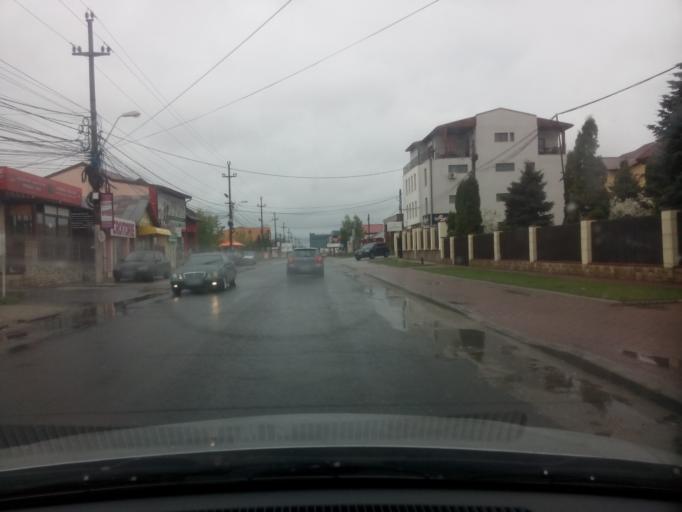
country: RO
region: Ilfov
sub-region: Voluntari City
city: Voluntari
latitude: 44.5052
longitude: 26.1366
